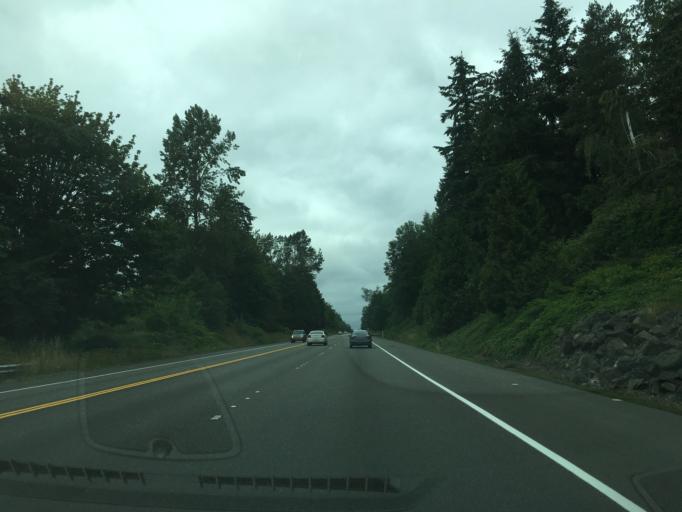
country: US
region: Washington
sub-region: Snohomish County
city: West Lake Stevens
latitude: 47.9915
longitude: -122.1267
